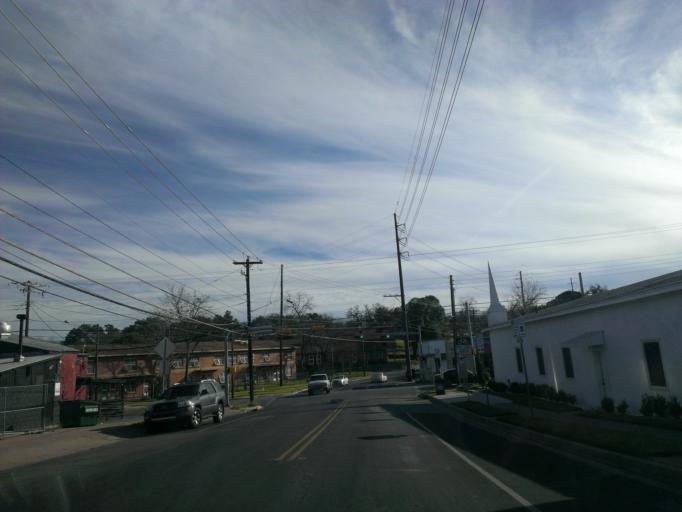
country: US
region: Texas
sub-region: Travis County
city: Austin
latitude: 30.2704
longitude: -97.7193
